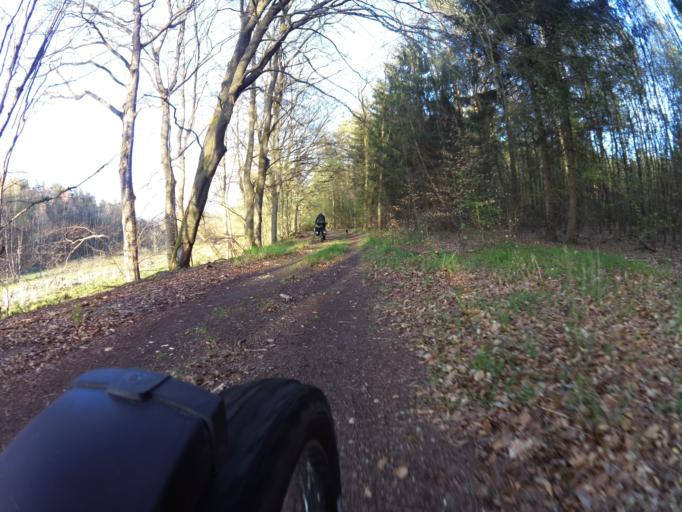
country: PL
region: West Pomeranian Voivodeship
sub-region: Powiat gryficki
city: Ploty
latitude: 53.7521
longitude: 15.2974
